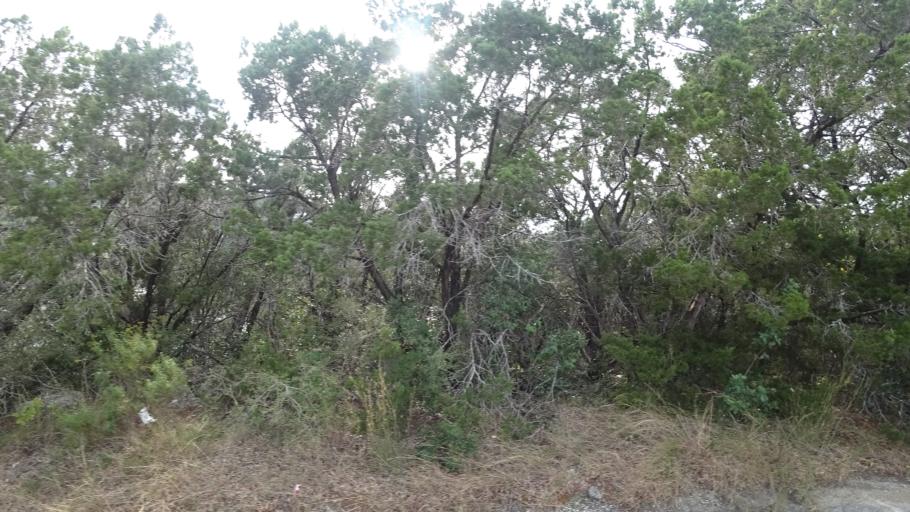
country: US
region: Texas
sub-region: Travis County
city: Hudson Bend
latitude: 30.3969
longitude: -97.8806
